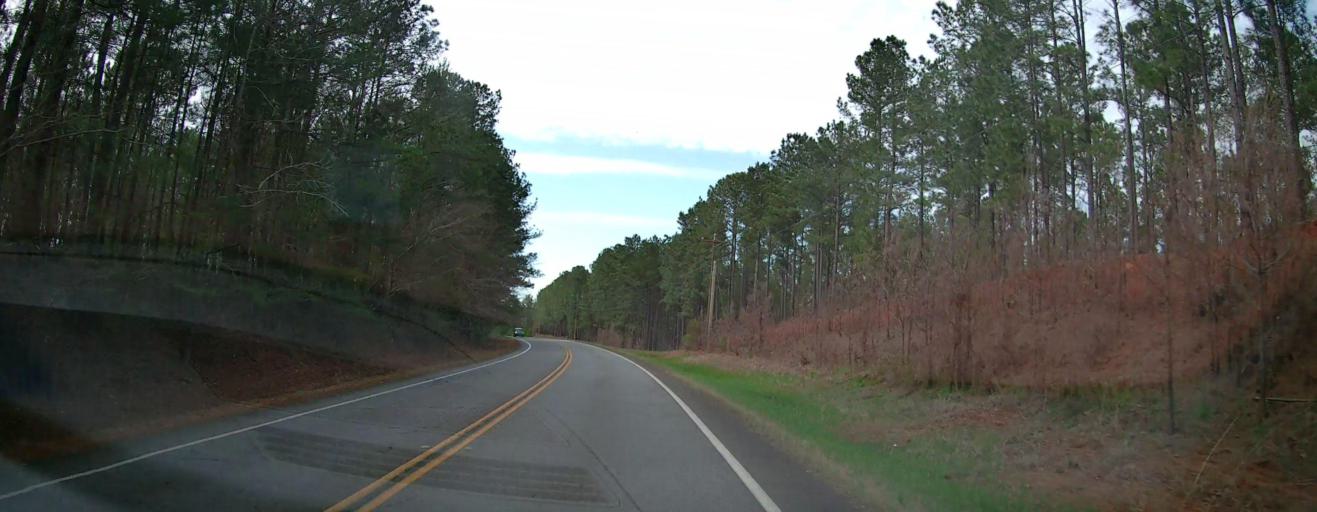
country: US
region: Georgia
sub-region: Jones County
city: Gray
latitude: 32.9946
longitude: -83.6874
